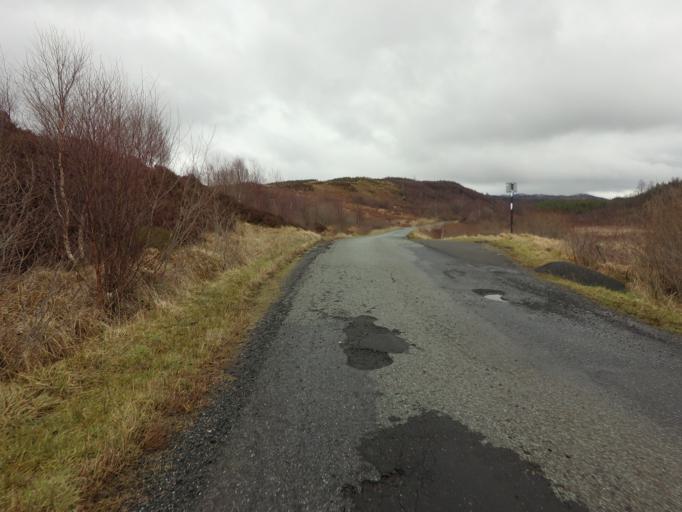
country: GB
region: Scotland
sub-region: West Dunbartonshire
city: Balloch
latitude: 56.2453
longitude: -4.5778
